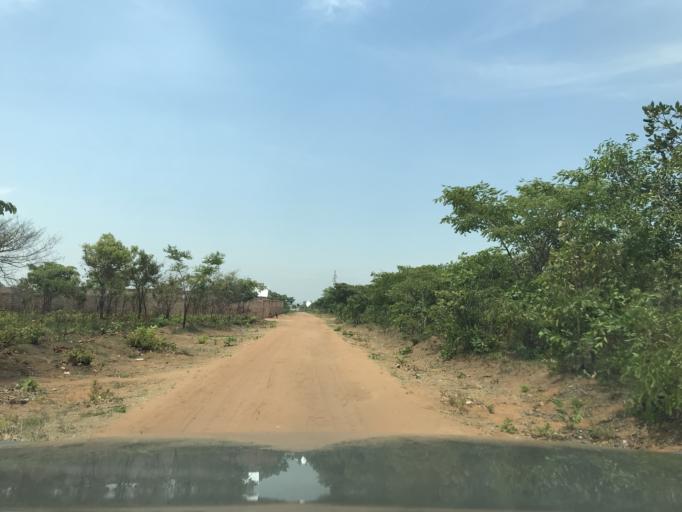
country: ZM
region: Northern
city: Kasama
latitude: -10.2218
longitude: 31.1235
